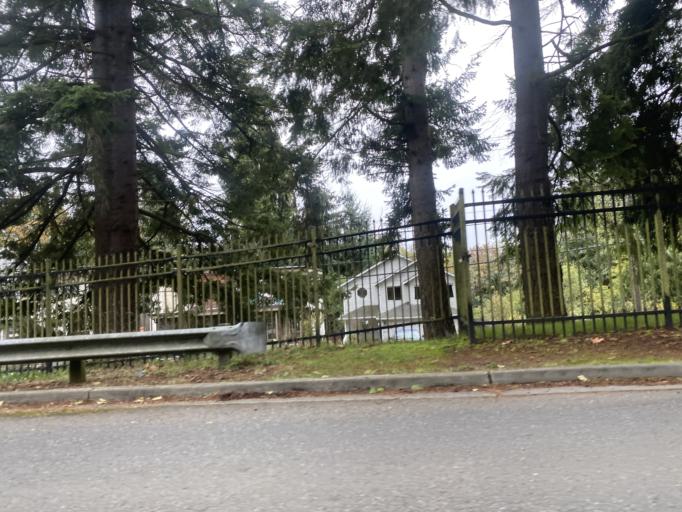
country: US
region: Washington
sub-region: King County
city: Seattle
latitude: 47.6606
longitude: -122.4039
